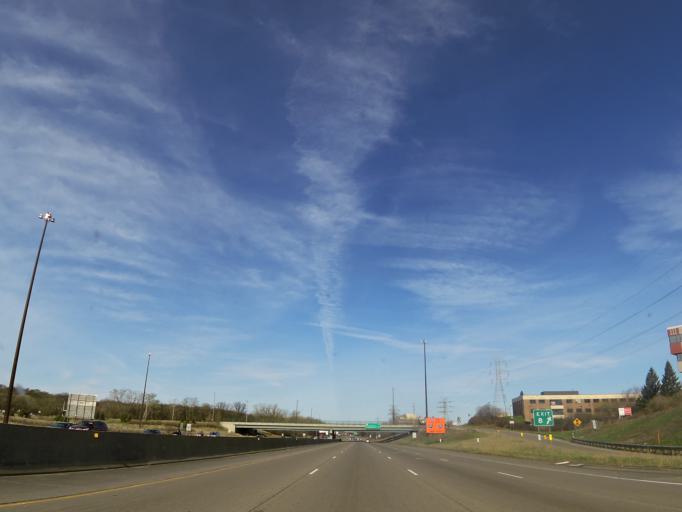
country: US
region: Minnesota
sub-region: Hennepin County
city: Edina
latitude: 44.8596
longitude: -93.3587
